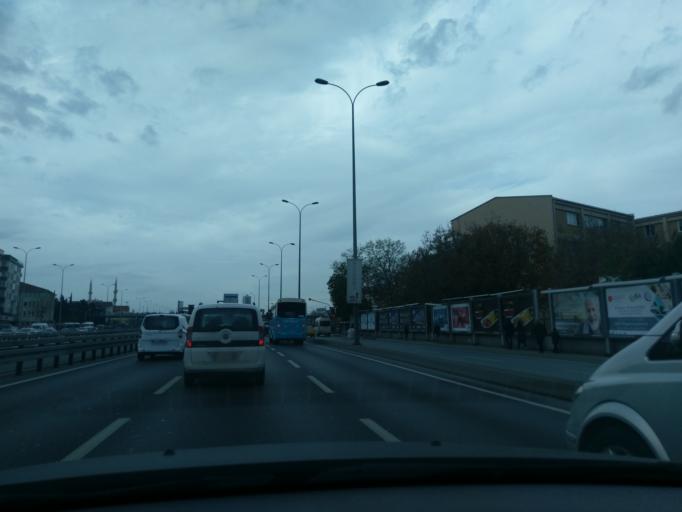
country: TR
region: Istanbul
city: Yakuplu
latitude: 40.9824
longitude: 28.7282
